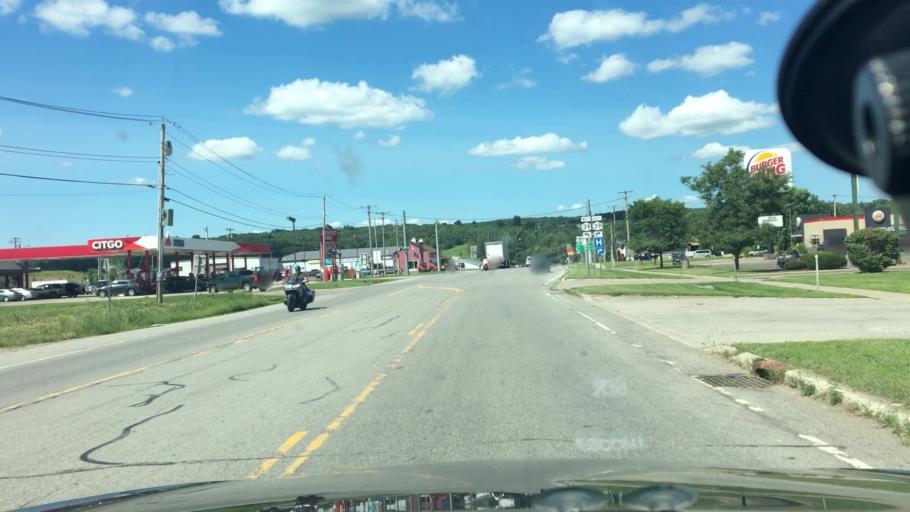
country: US
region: New York
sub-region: Erie County
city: Springville
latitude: 42.5079
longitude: -78.6893
